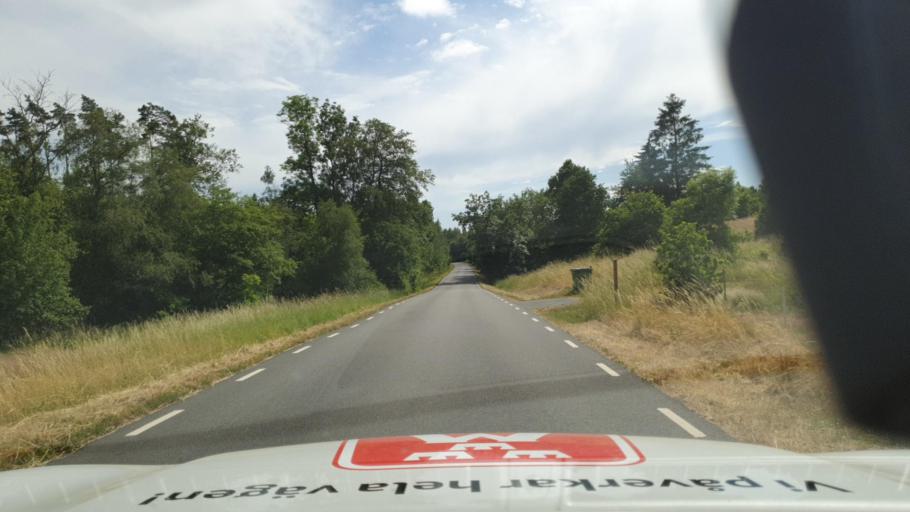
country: SE
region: Skane
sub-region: Tomelilla Kommun
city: Tomelilla
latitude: 55.7033
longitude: 13.9567
